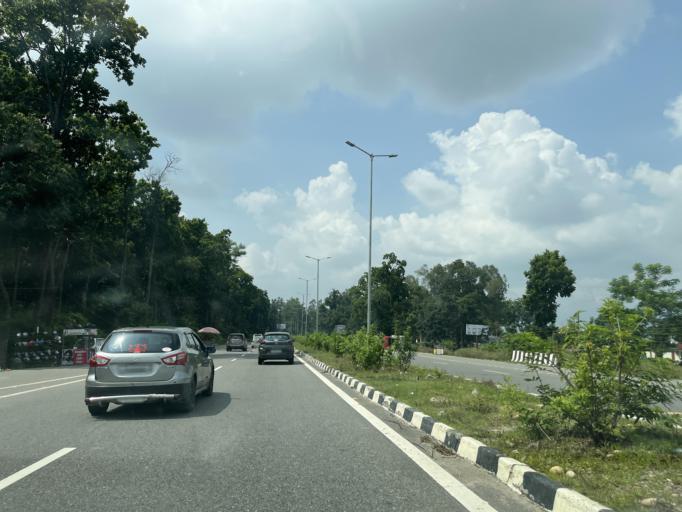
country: IN
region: Uttarakhand
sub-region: Dehradun
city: Raipur
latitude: 30.2480
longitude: 78.0957
